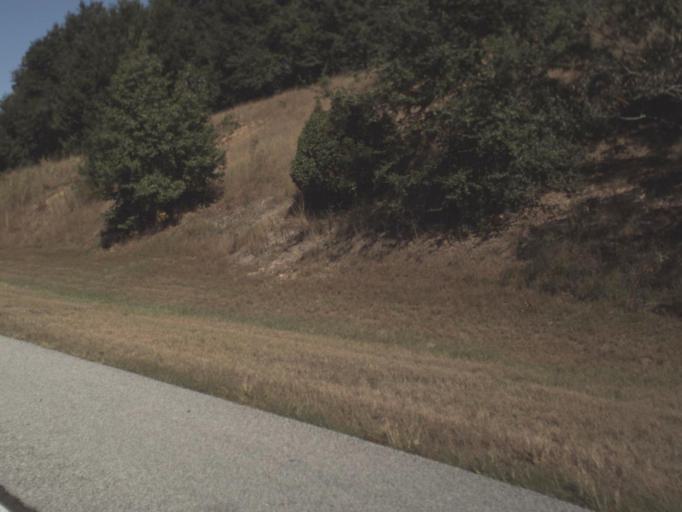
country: US
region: Florida
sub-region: Lake County
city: Montverde
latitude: 28.5724
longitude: -81.6962
